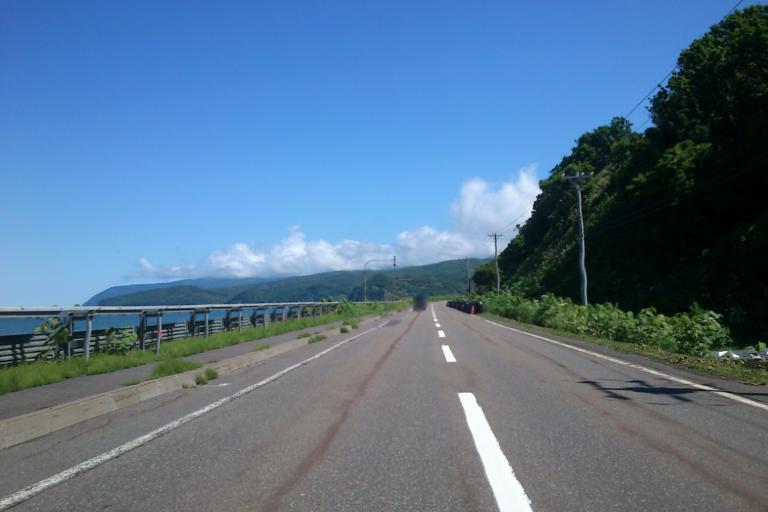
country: JP
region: Hokkaido
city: Ishikari
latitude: 43.5671
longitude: 141.3807
